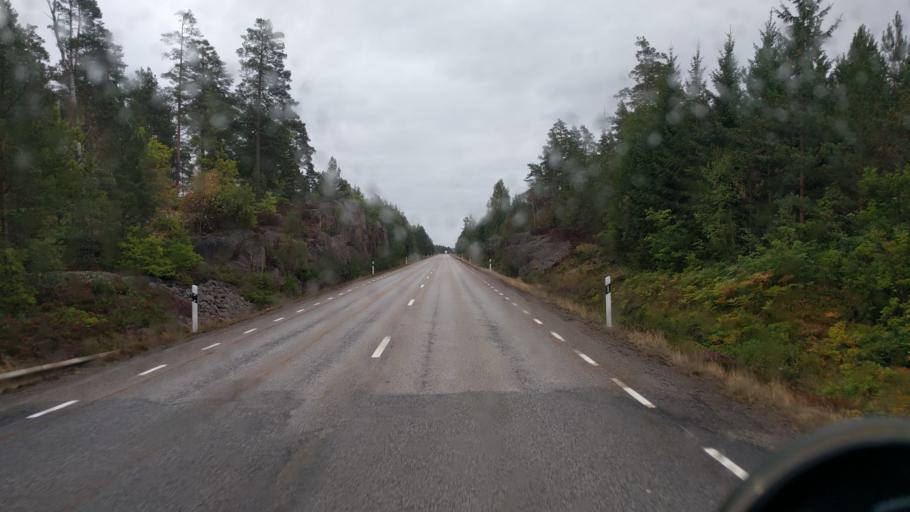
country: SE
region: Kalmar
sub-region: Vasterviks Kommun
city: Ankarsrum
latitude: 57.7001
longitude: 16.2534
